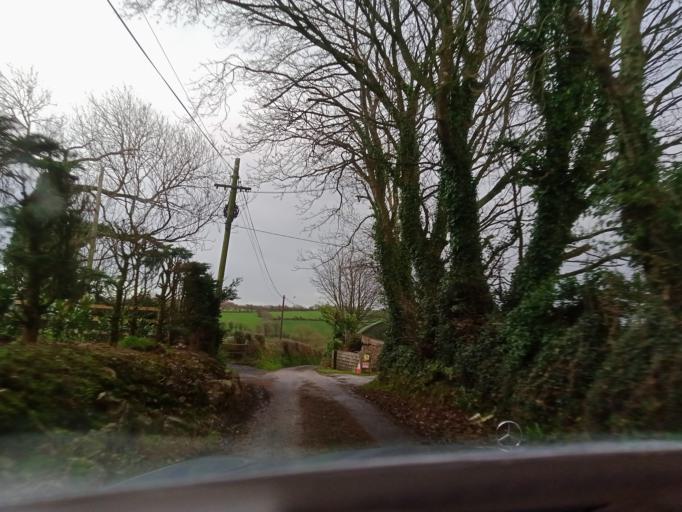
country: IE
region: Munster
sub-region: Waterford
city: Waterford
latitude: 52.3083
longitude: -7.0470
